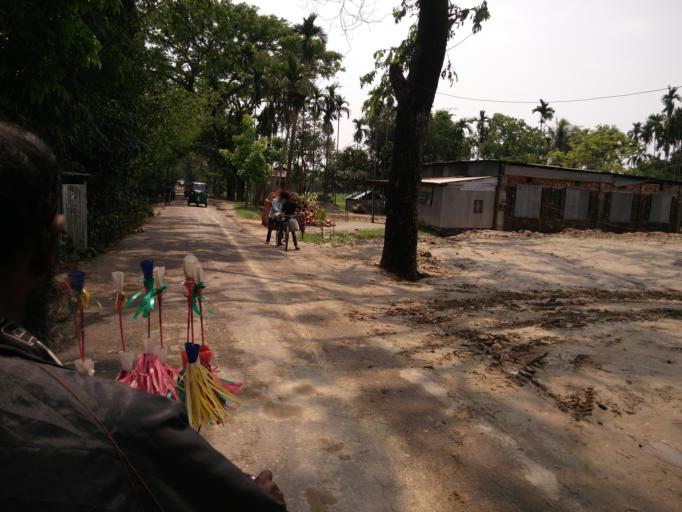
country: BD
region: Dhaka
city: Sherpur
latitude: 24.9438
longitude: 90.1602
